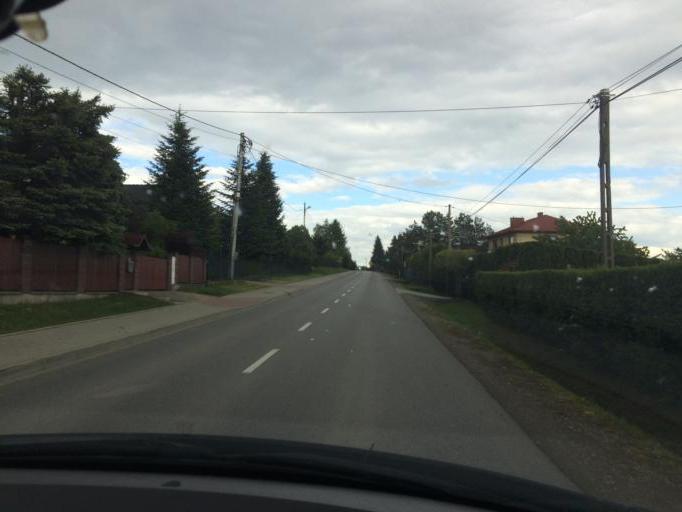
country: PL
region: Lesser Poland Voivodeship
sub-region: Powiat krakowski
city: Ochojno
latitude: 49.9745
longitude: 20.0066
